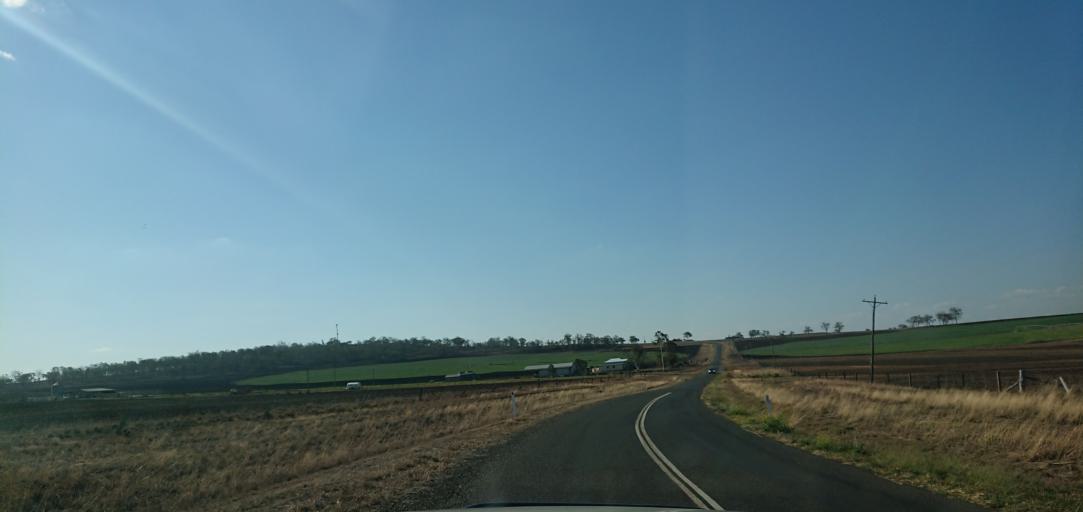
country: AU
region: Queensland
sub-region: Toowoomba
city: Westbrook
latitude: -27.7104
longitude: 151.7160
